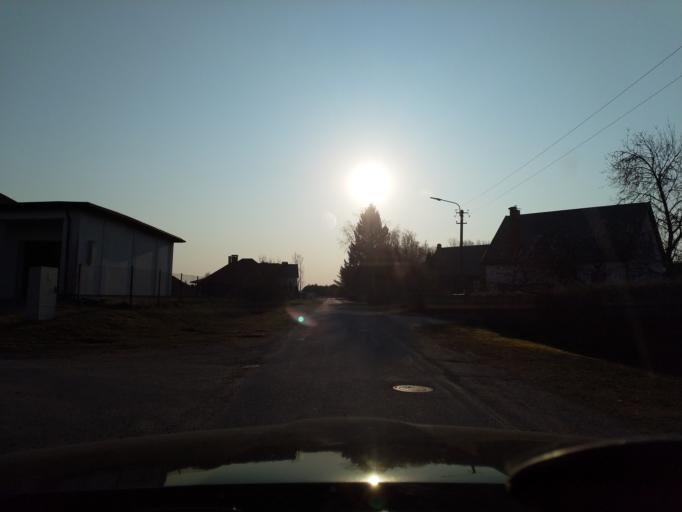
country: LV
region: Grobina
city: Grobina
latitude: 56.5330
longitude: 21.1868
